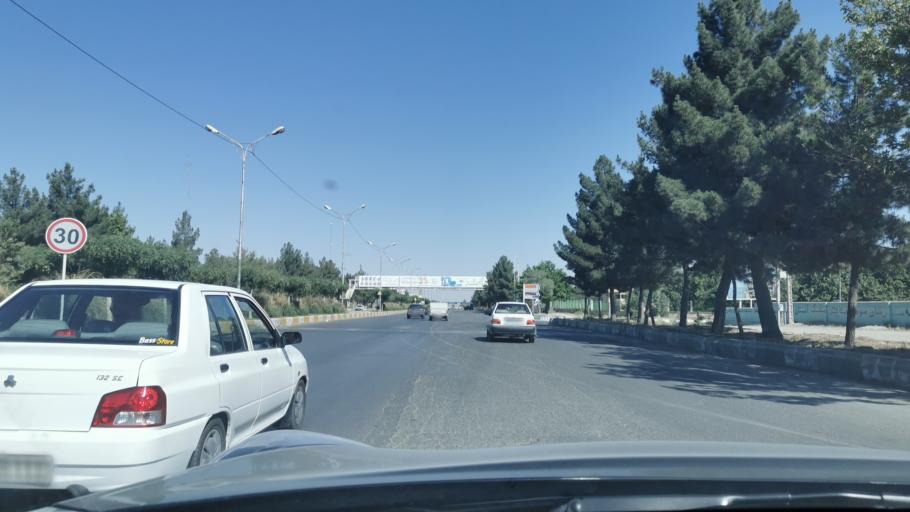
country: IR
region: Razavi Khorasan
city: Chenaran
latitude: 36.6371
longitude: 59.1250
